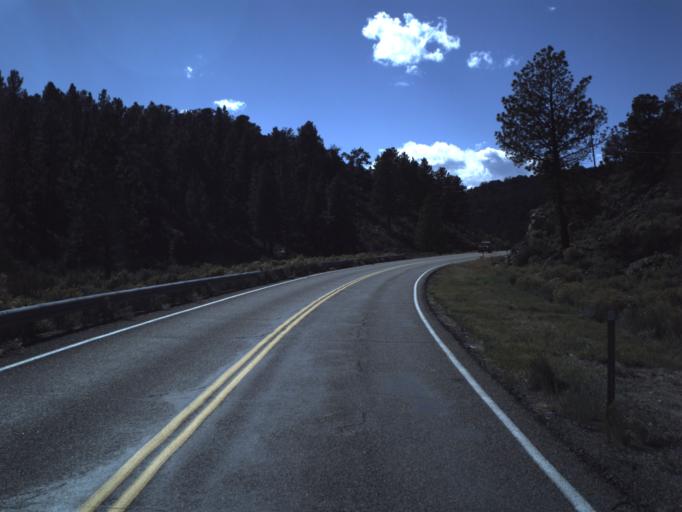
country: US
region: Utah
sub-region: Garfield County
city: Panguitch
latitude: 37.7688
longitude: -112.4520
